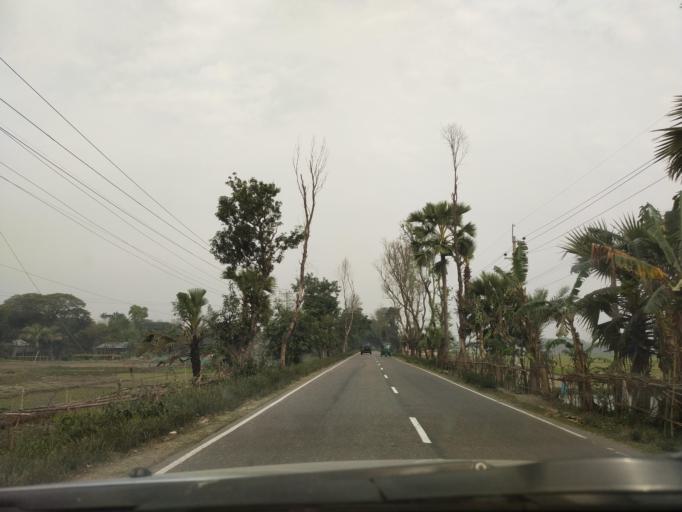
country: BD
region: Dhaka
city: Narsingdi
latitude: 24.0005
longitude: 90.7377
